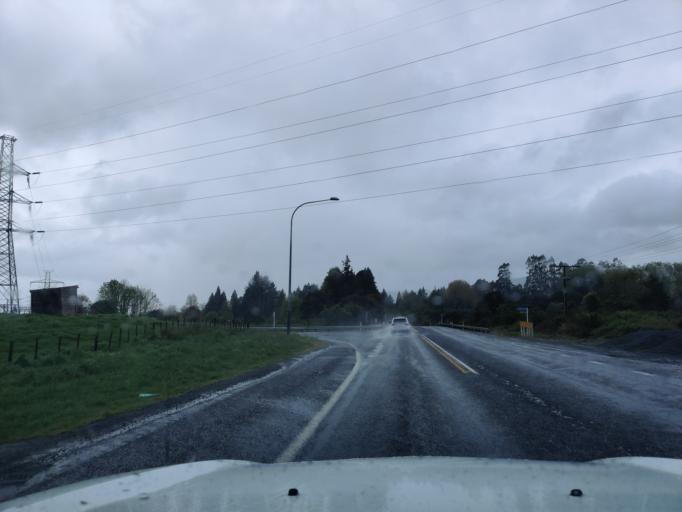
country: NZ
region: Bay of Plenty
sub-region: Rotorua District
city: Rotorua
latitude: -38.0743
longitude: 176.1553
